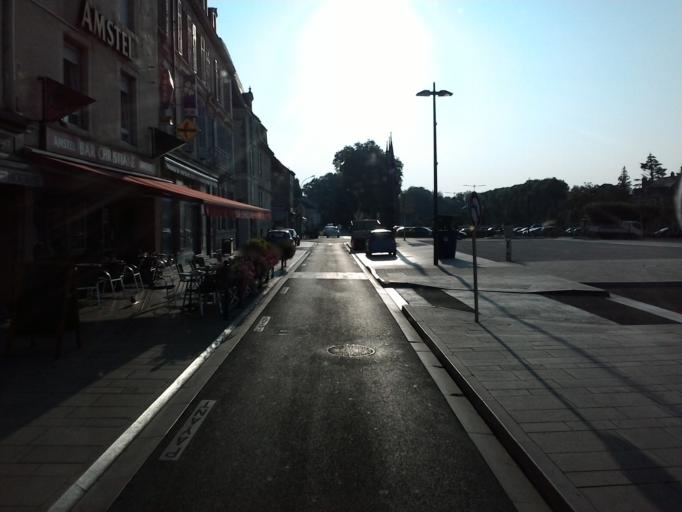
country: FR
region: Franche-Comte
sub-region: Departement de la Haute-Saone
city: Vesoul
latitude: 47.6226
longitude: 6.1590
